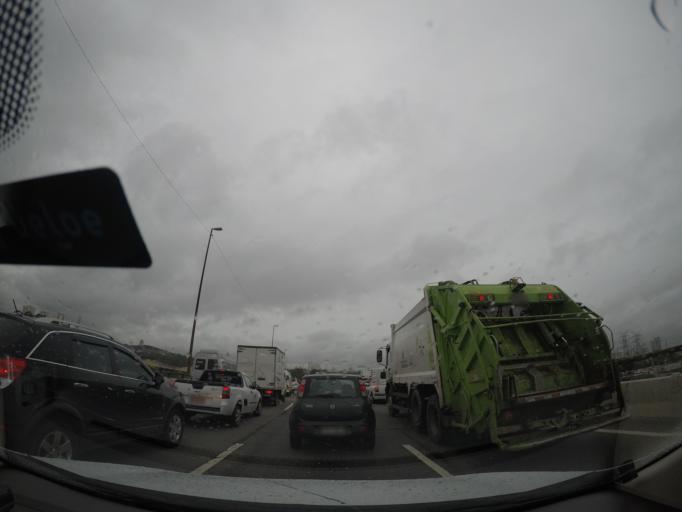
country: BR
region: Sao Paulo
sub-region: Osasco
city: Osasco
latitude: -23.5260
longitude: -46.7514
